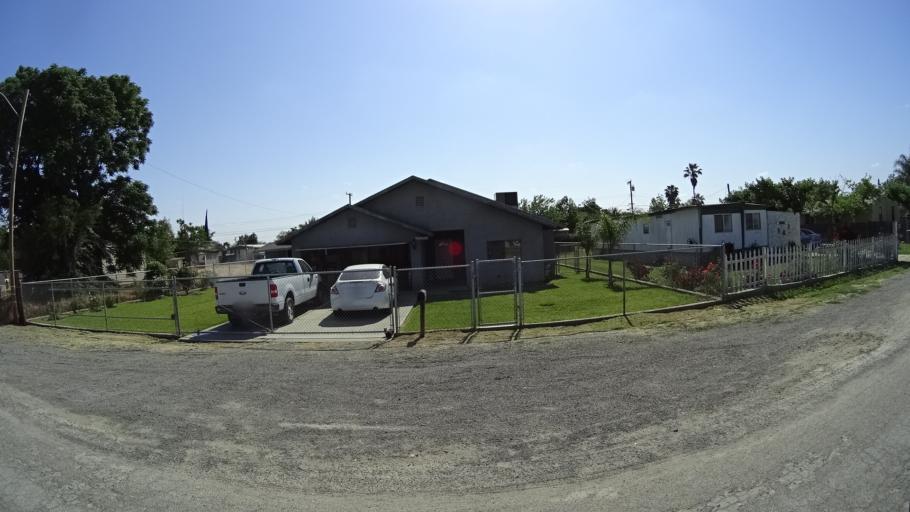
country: US
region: California
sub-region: Kings County
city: Home Garden
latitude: 36.3003
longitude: -119.6340
